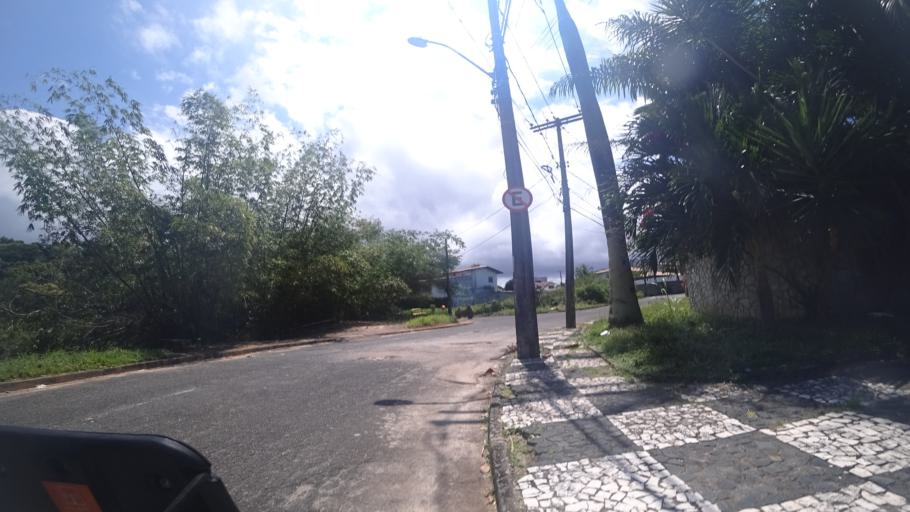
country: BR
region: Bahia
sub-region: Salvador
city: Salvador
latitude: -12.9950
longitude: -38.4668
